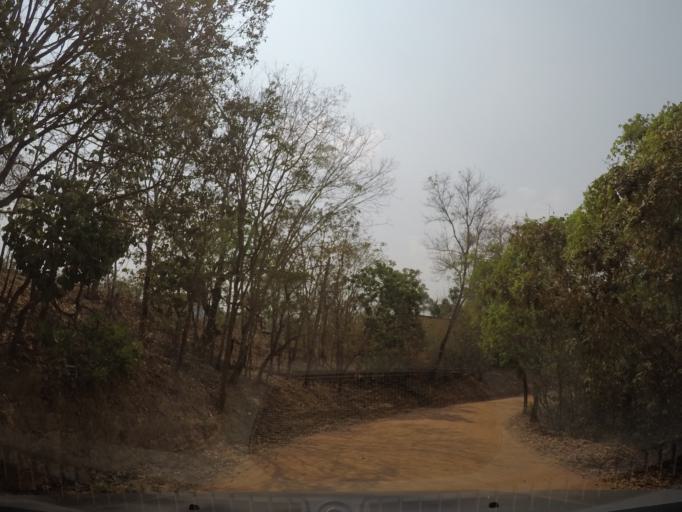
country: BR
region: Goias
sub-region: Pirenopolis
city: Pirenopolis
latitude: -15.8399
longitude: -48.9569
